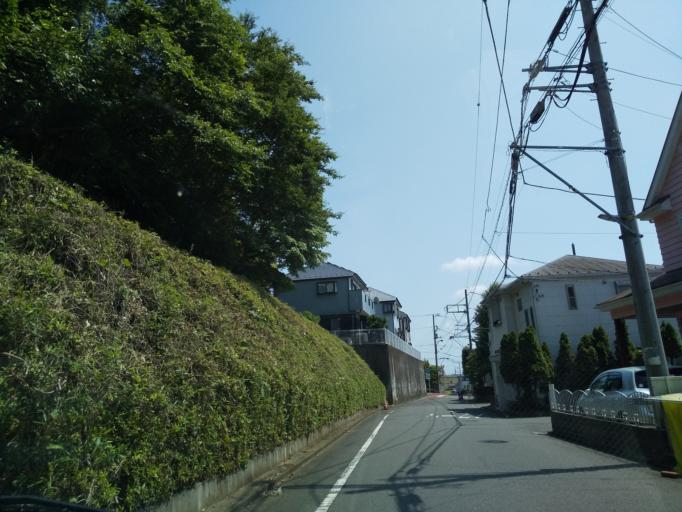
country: JP
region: Kanagawa
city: Zama
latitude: 35.4979
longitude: 139.3909
